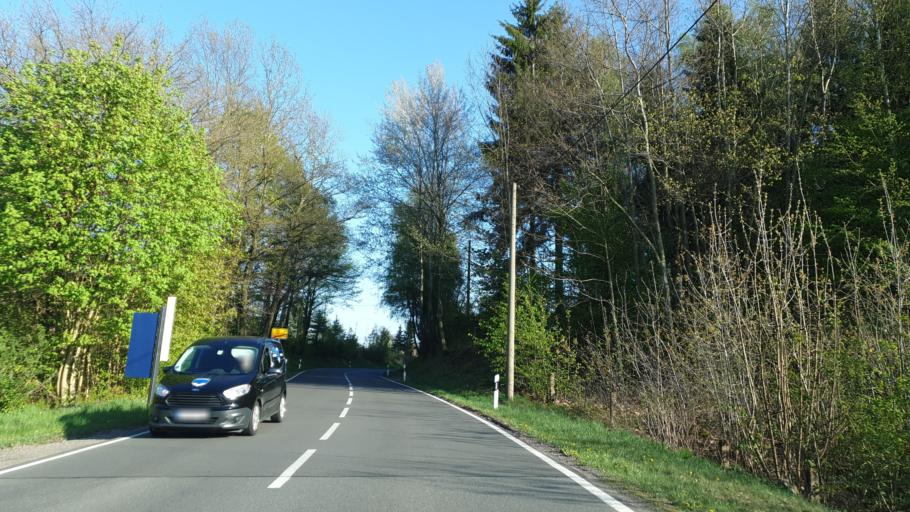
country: DE
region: Saxony
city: Schlema
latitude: 50.6059
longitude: 12.6903
